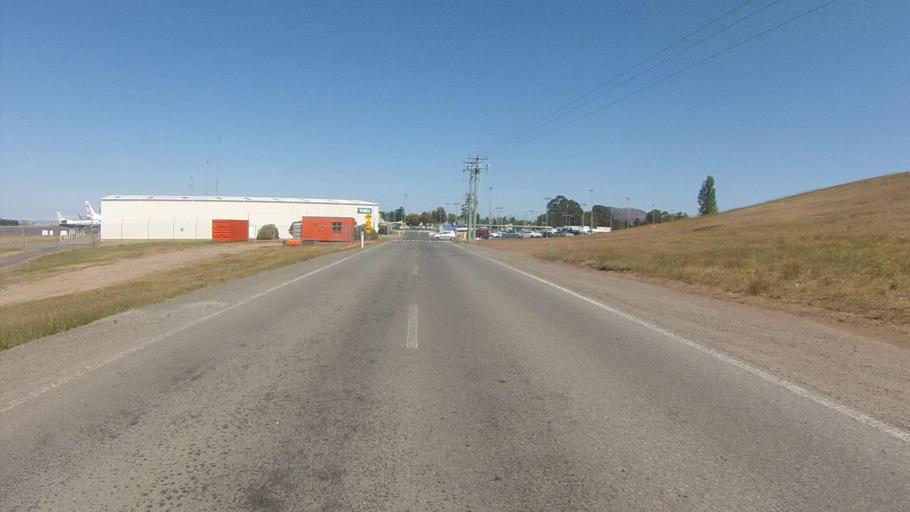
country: AU
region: Tasmania
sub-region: Clarence
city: Seven Mile Beach
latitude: -42.8348
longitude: 147.5030
